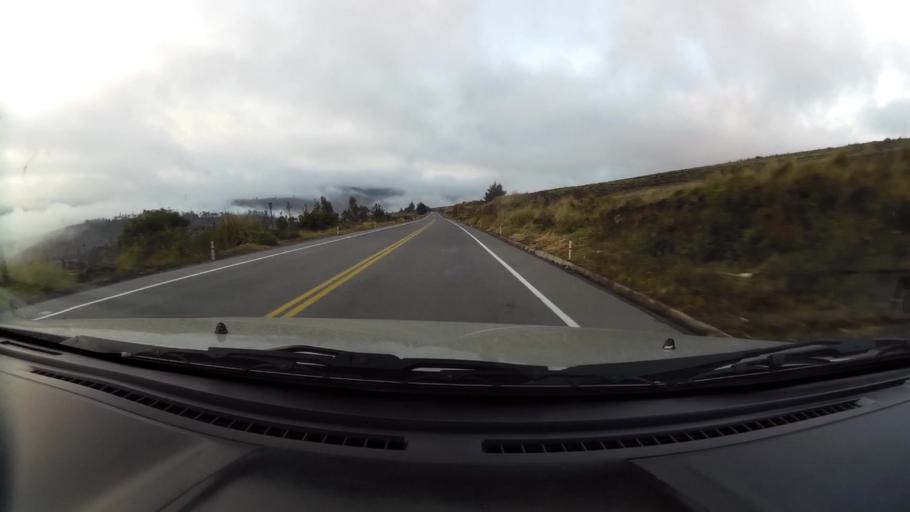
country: EC
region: Chimborazo
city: Alausi
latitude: -2.1062
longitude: -78.7489
